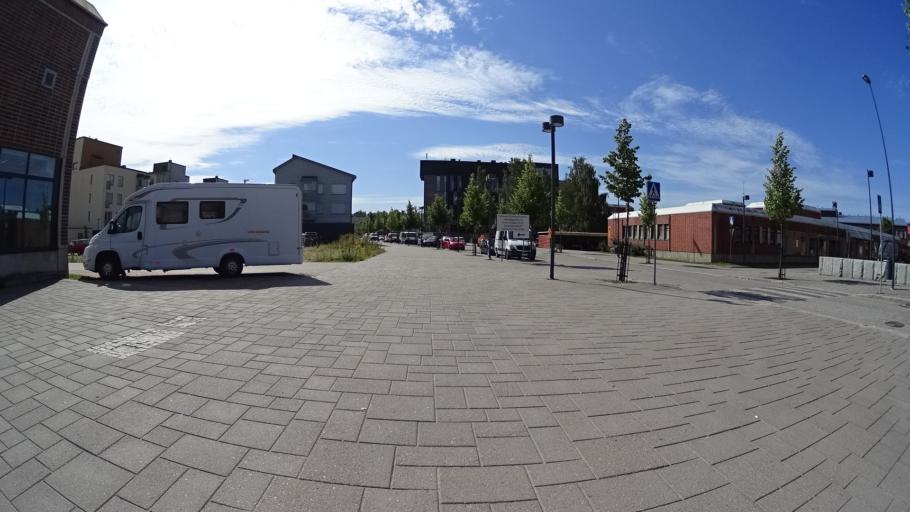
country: FI
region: Uusimaa
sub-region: Helsinki
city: Kirkkonummi
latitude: 60.1232
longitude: 24.4398
